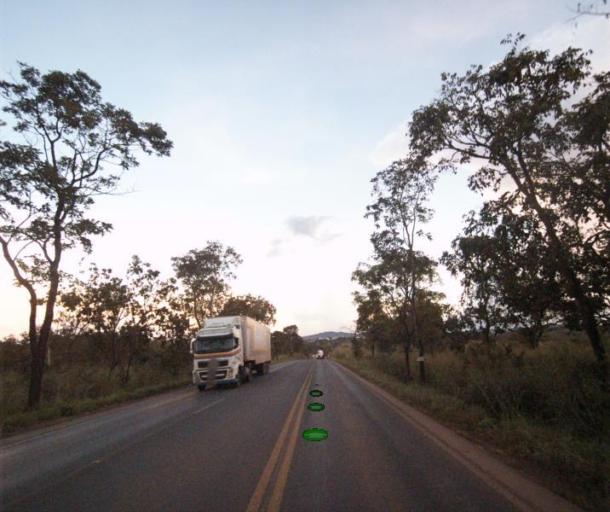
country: BR
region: Goias
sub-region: Uruacu
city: Uruacu
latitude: -14.4926
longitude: -49.1525
